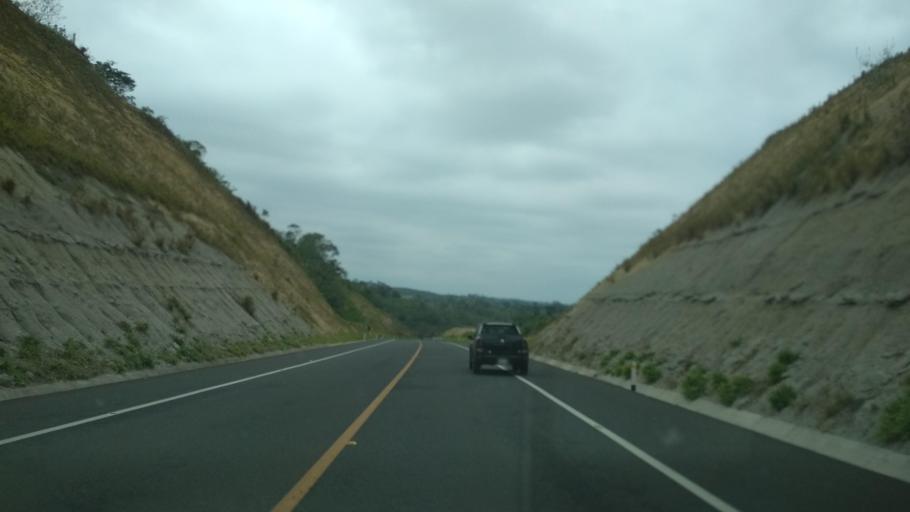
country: MX
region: Veracruz
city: Agua Dulce
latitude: 20.4232
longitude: -97.2210
